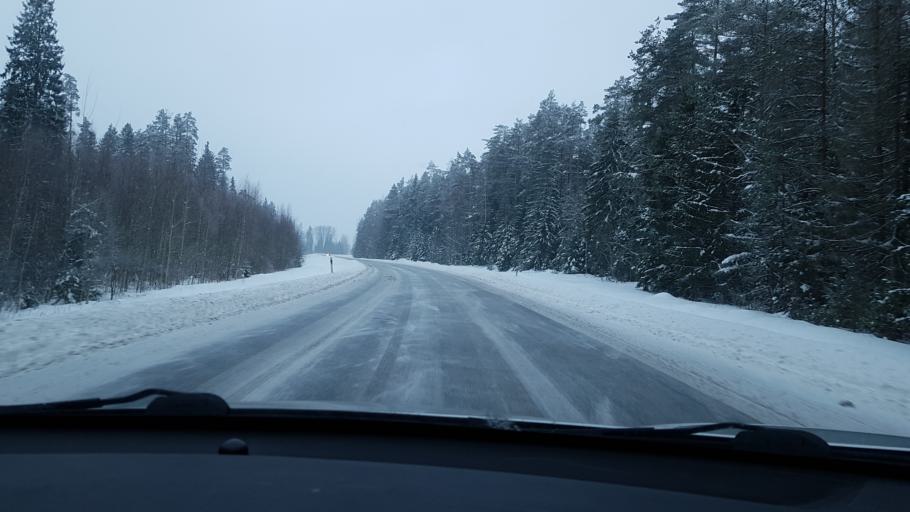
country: EE
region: Jaervamaa
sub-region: Tueri vald
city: Sarevere
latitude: 58.7412
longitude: 25.3031
